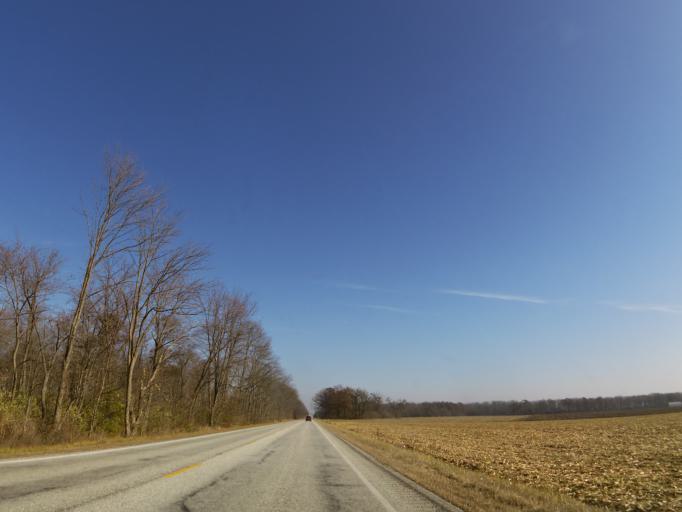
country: US
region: Indiana
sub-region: Shelby County
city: Shelbyville
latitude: 39.5456
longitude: -85.6905
